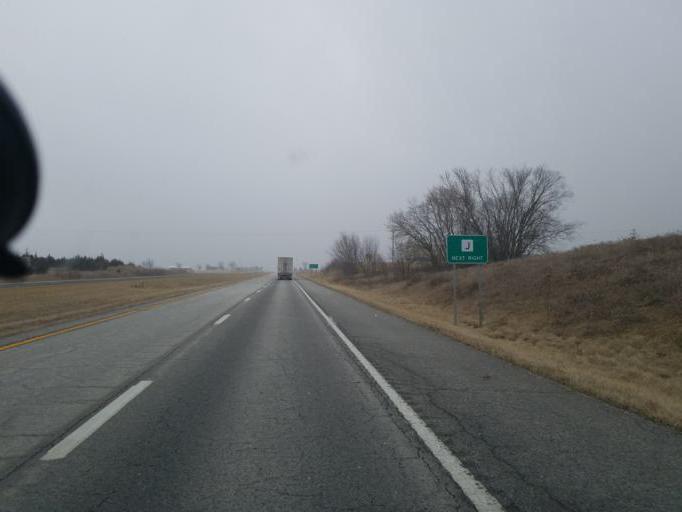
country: US
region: Missouri
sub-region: Macon County
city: La Plata
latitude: 39.9214
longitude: -92.4750
